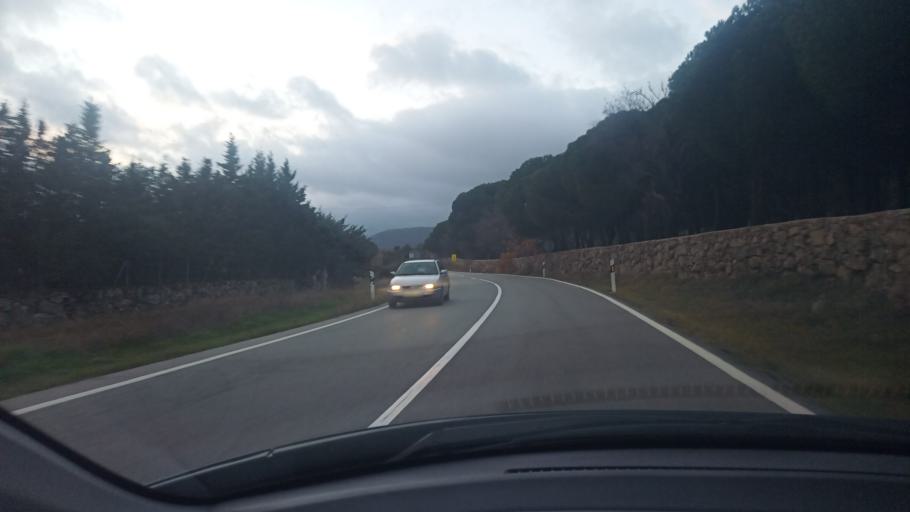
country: ES
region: Madrid
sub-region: Provincia de Madrid
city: Zarzalejo
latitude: 40.5408
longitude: -4.1454
